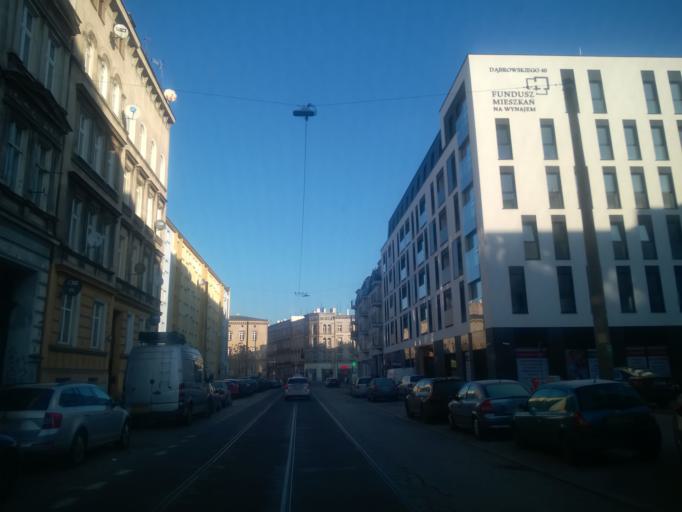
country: PL
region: Lower Silesian Voivodeship
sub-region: Powiat wroclawski
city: Wroclaw
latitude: 51.0999
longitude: 17.0410
